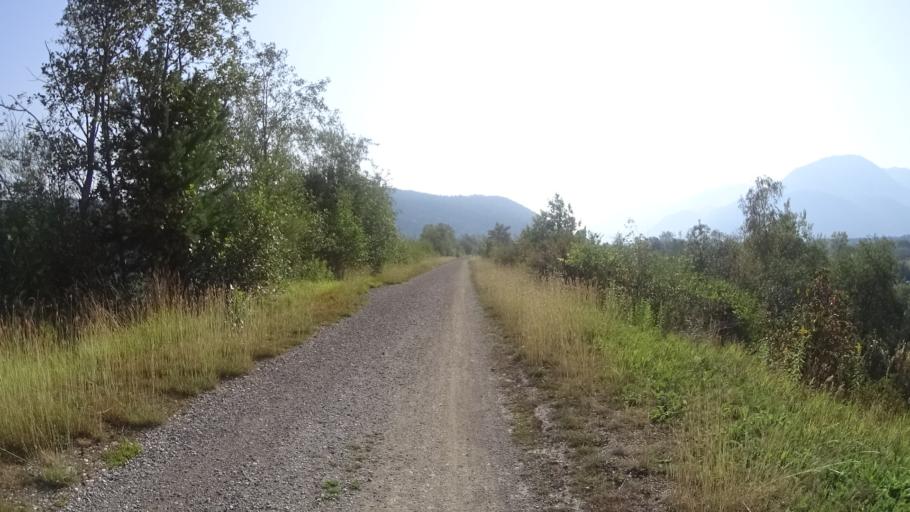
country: AT
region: Carinthia
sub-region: Politischer Bezirk Klagenfurt Land
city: Maria Rain
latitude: 46.5470
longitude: 14.2835
